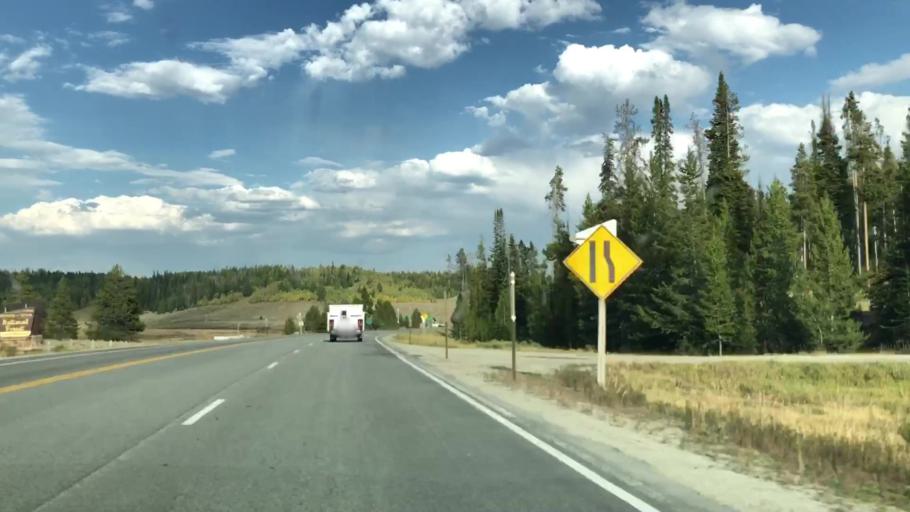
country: US
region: Wyoming
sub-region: Sublette County
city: Pinedale
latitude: 43.1325
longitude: -110.2009
